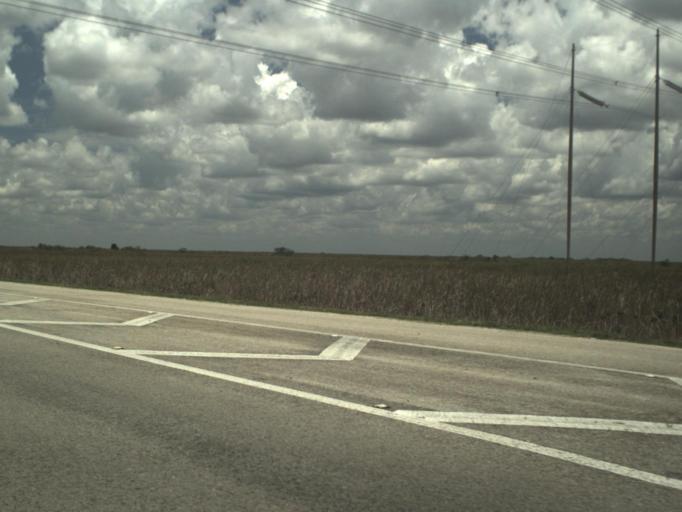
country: US
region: Florida
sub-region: Broward County
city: Weston
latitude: 26.1459
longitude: -80.4496
